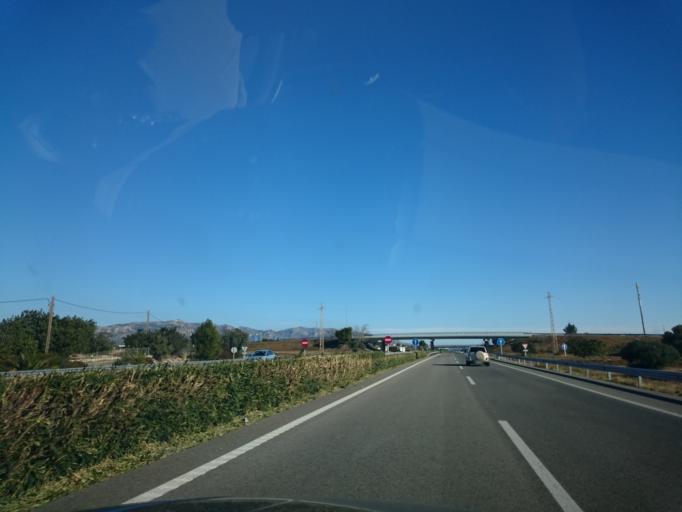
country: ES
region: Catalonia
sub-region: Provincia de Tarragona
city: l'Ametlla de Mar
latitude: 40.8833
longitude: 0.7959
